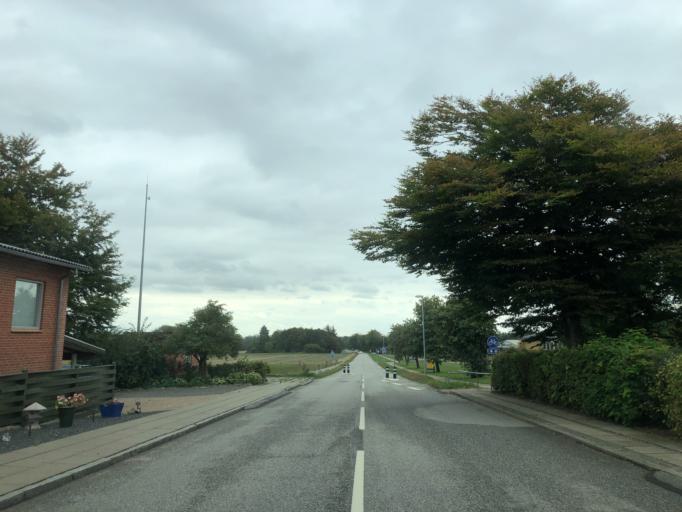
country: DK
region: Central Jutland
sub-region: Herning Kommune
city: Vildbjerg
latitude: 56.1794
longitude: 8.8345
